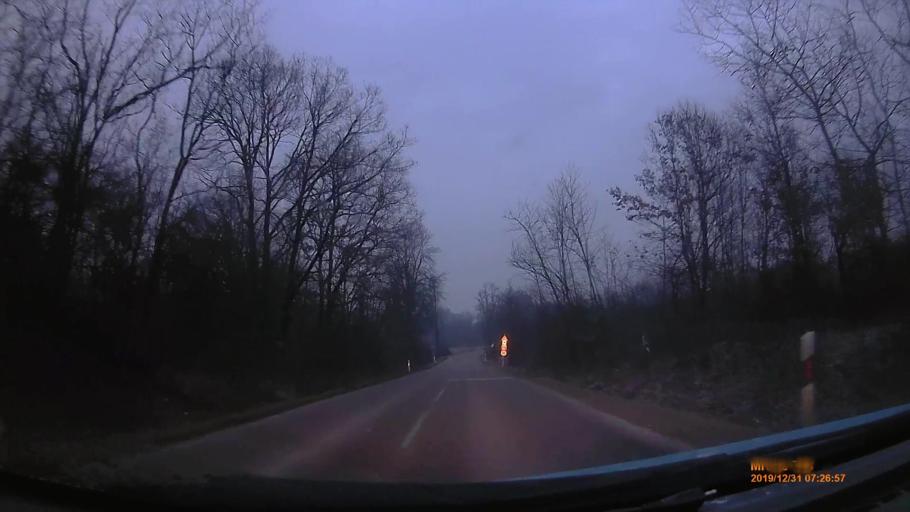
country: HU
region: Heves
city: Matraderecske
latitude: 47.9249
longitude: 20.0780
